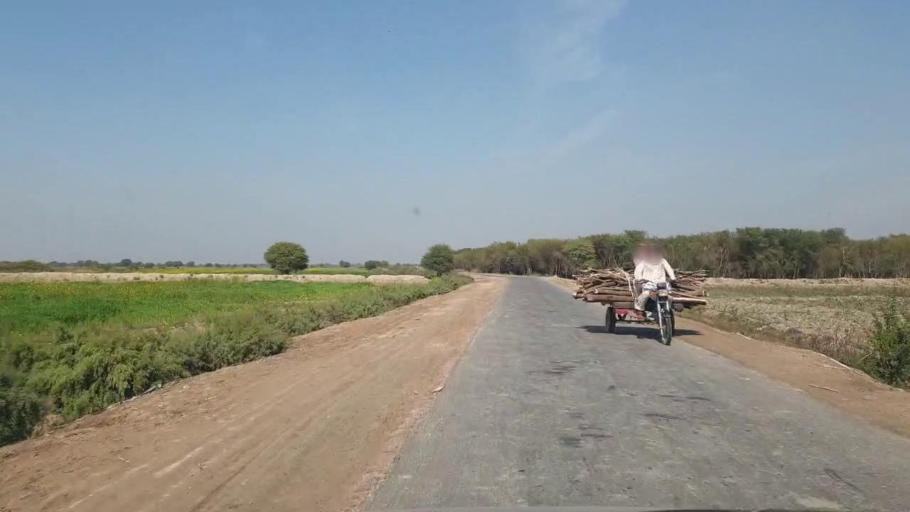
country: PK
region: Sindh
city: Chambar
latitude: 25.3136
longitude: 68.8174
